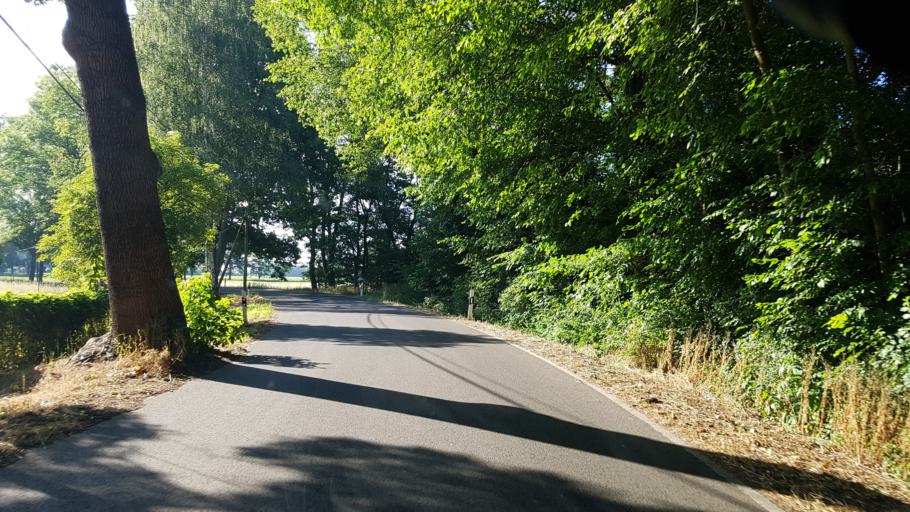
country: DE
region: Brandenburg
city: Golssen
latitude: 51.9522
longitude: 13.6476
